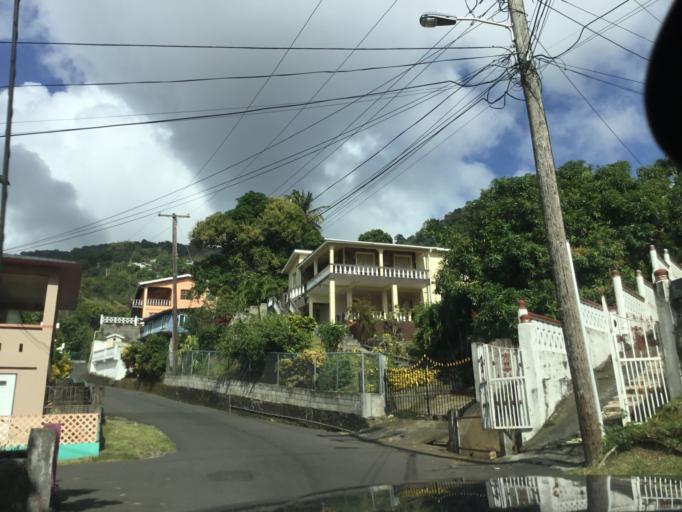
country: VC
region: Saint George
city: Kingstown
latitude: 13.1606
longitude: -61.2194
